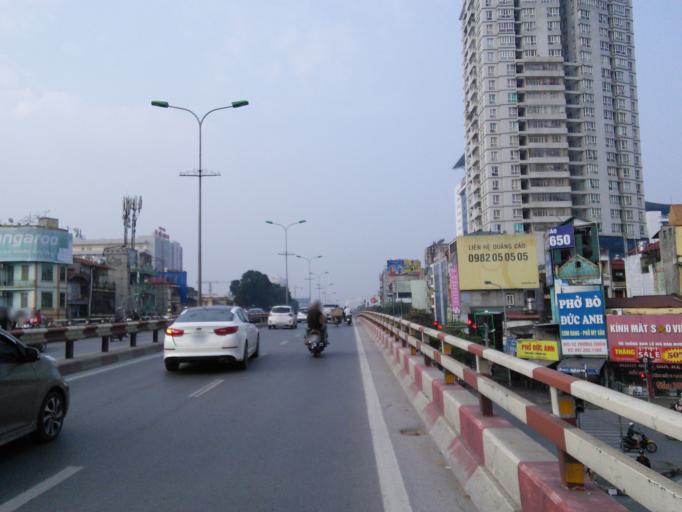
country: VN
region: Ha Noi
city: Hai BaTrung
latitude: 20.9974
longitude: 105.8414
